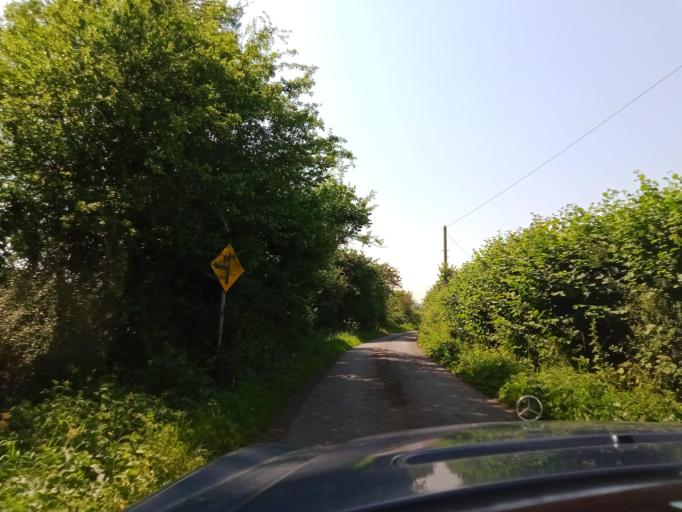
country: IE
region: Leinster
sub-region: Kilkenny
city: Mooncoin
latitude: 52.3110
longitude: -7.2772
